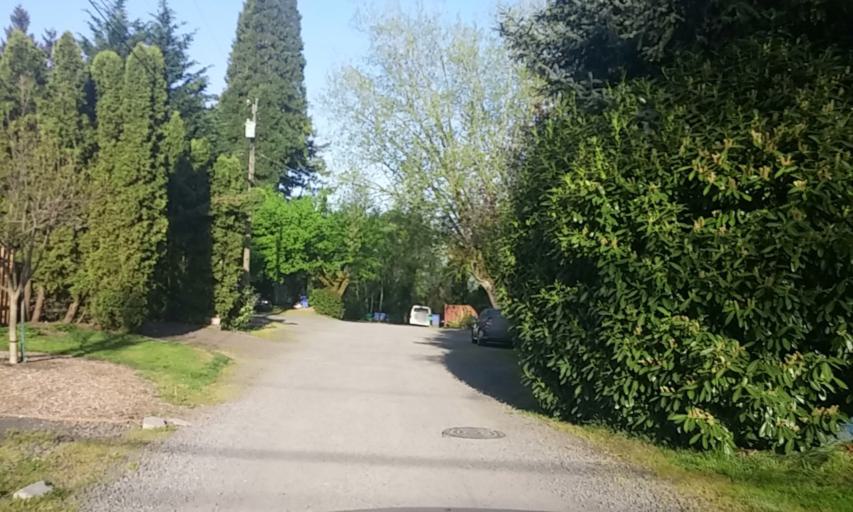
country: US
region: Oregon
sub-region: Washington County
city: Metzger
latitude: 45.4447
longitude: -122.7313
